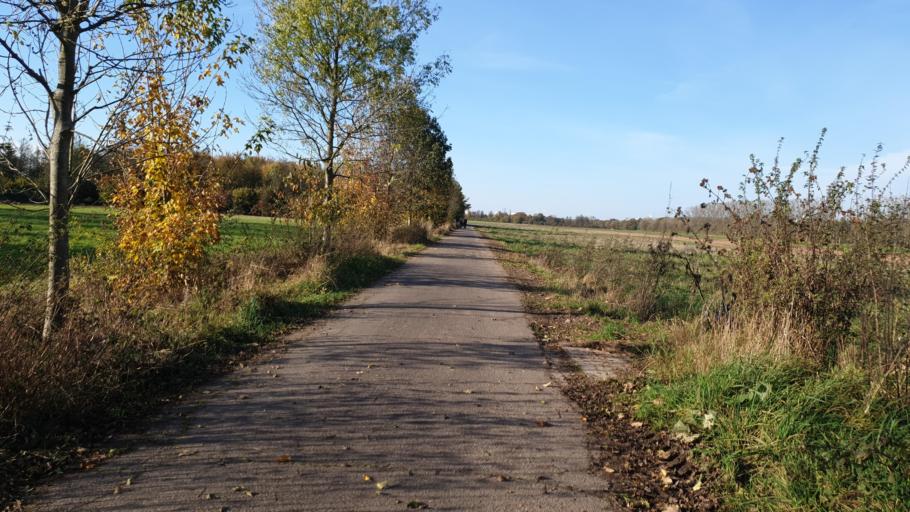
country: DE
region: North Rhine-Westphalia
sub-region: Regierungsbezirk Koln
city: Kerpen
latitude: 50.9149
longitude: 6.6974
